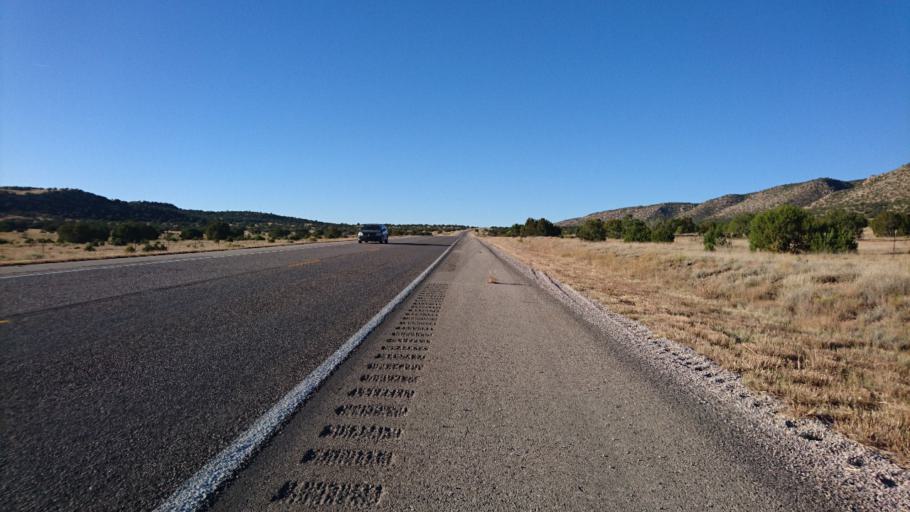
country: US
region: New Mexico
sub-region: Cibola County
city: Grants
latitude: 35.0123
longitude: -107.8892
